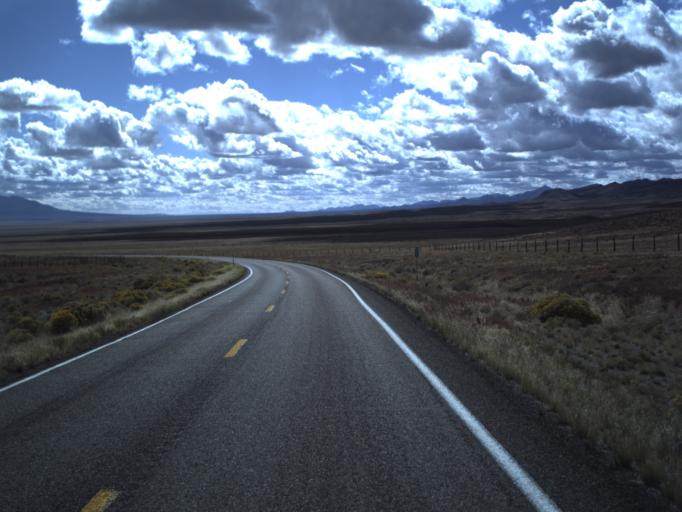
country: US
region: Utah
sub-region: Beaver County
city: Milford
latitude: 38.6057
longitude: -113.8348
